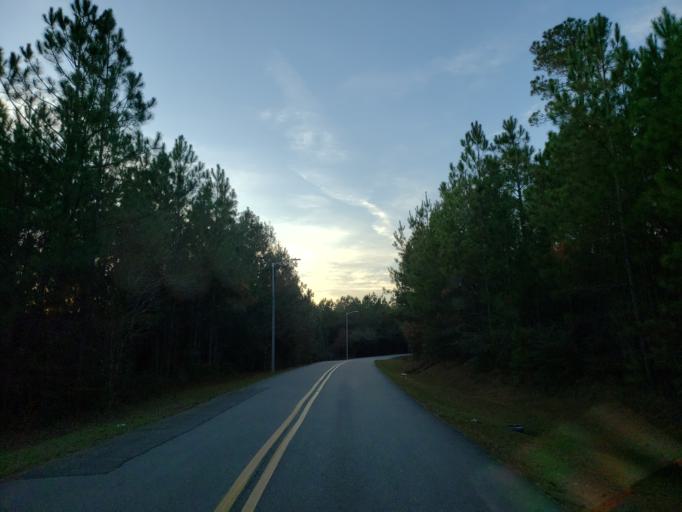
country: US
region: Mississippi
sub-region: Forrest County
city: Hattiesburg
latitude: 31.2786
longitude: -89.3101
